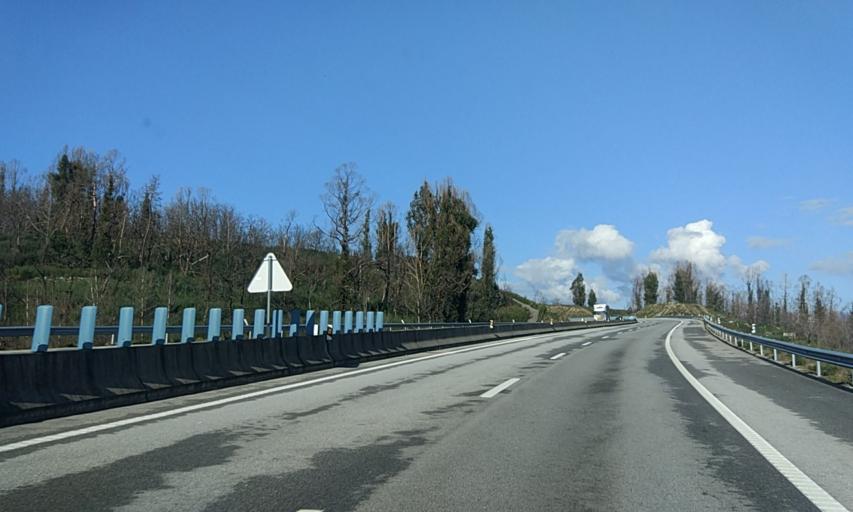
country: PT
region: Viseu
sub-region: Vouzela
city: Vouzela
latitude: 40.6988
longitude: -8.1003
